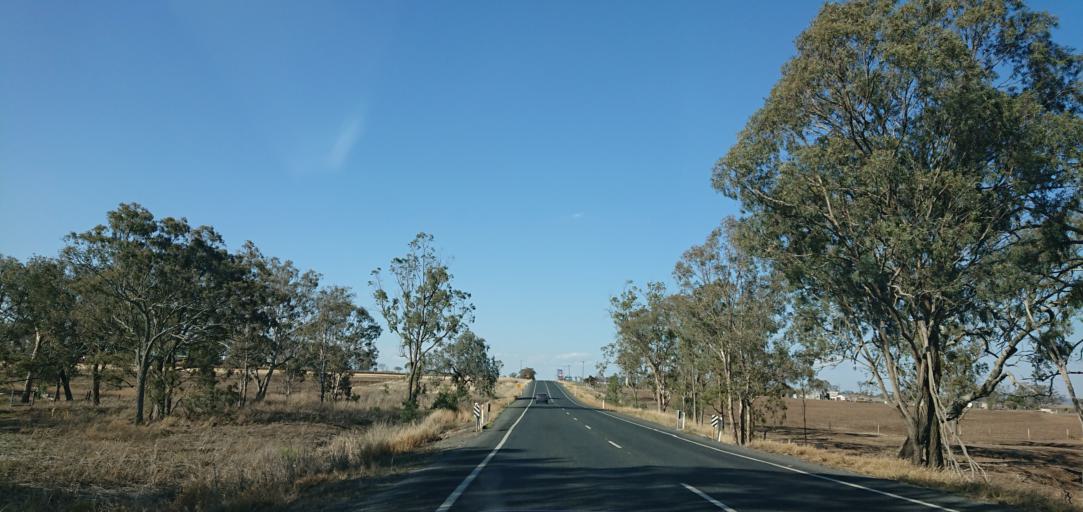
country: AU
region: Queensland
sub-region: Toowoomba
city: Westbrook
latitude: -27.6407
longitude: 151.7376
